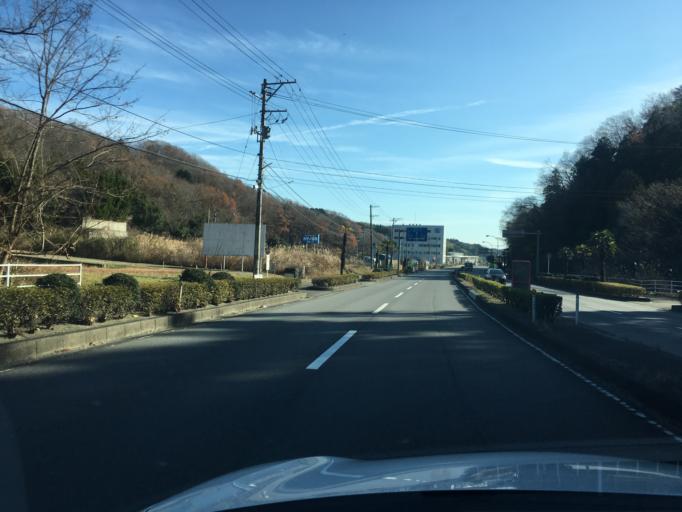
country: JP
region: Fukushima
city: Iwaki
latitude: 37.0003
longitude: 140.8207
